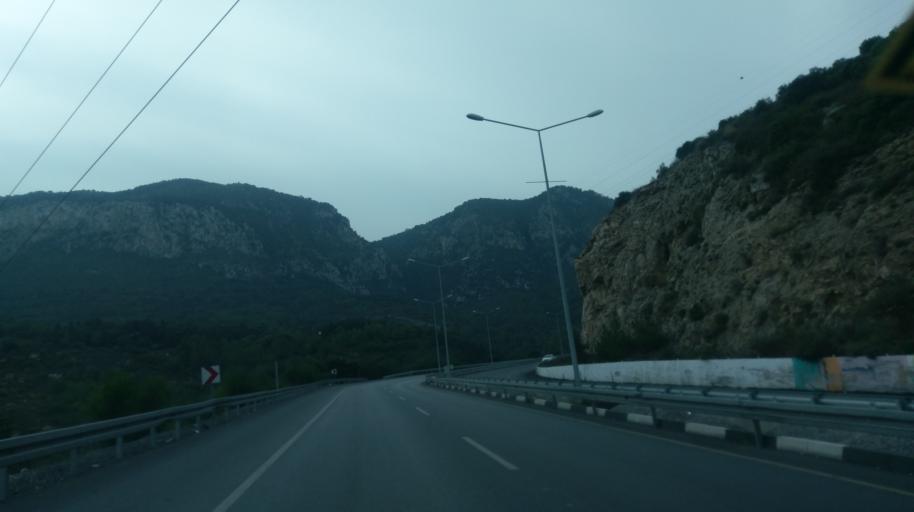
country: CY
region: Keryneia
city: Kyrenia
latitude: 35.3114
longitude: 33.3239
